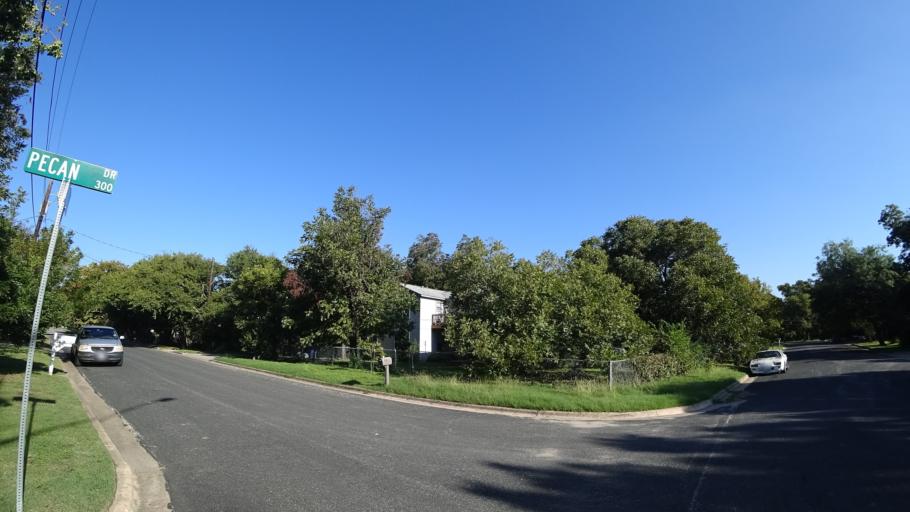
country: US
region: Texas
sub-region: Travis County
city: Austin
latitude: 30.3502
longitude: -97.6986
